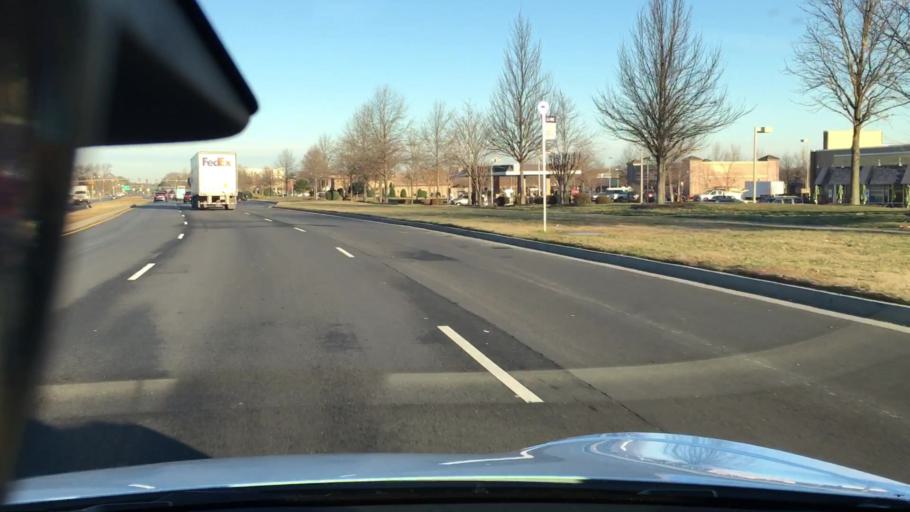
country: US
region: Virginia
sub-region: Henrico County
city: Montrose
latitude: 37.5243
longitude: -77.3530
